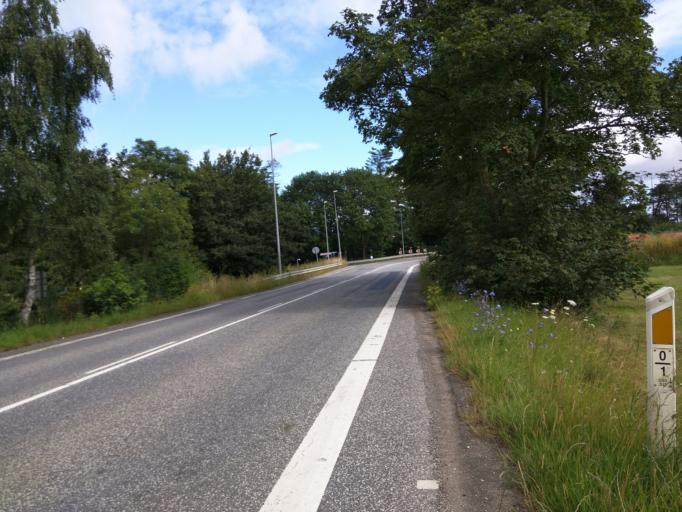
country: DK
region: Zealand
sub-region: Kalundborg Kommune
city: Svebolle
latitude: 55.6747
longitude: 11.2951
